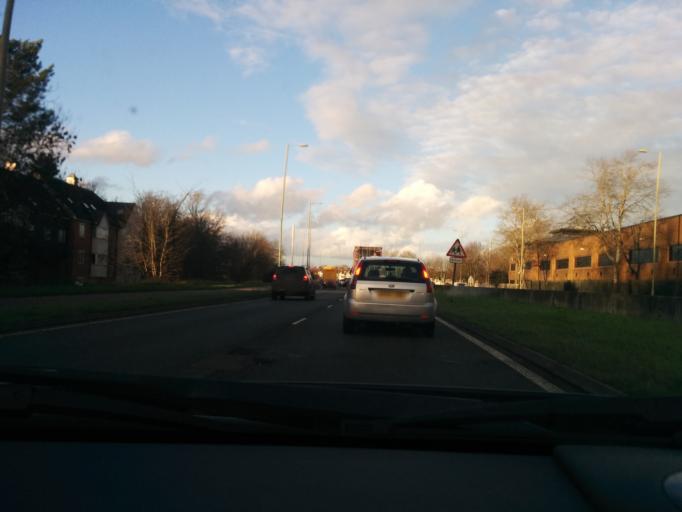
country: GB
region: England
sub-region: Oxfordshire
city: Cowley
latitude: 51.7577
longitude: -1.1947
